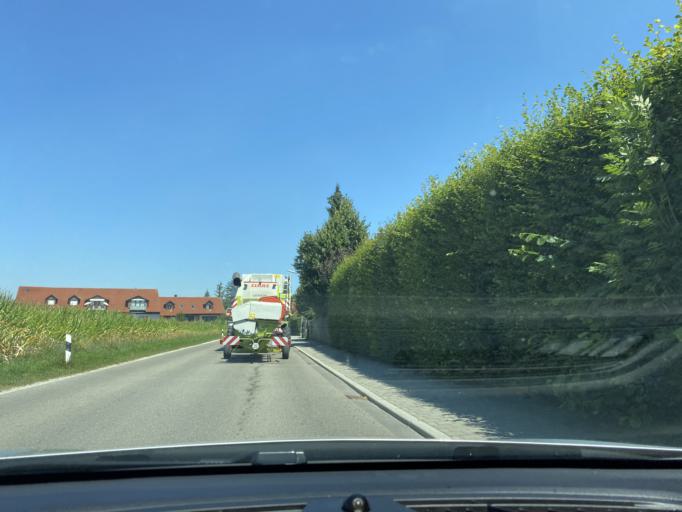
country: DE
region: Bavaria
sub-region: Upper Bavaria
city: Moosinning
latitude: 48.2697
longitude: 11.8453
